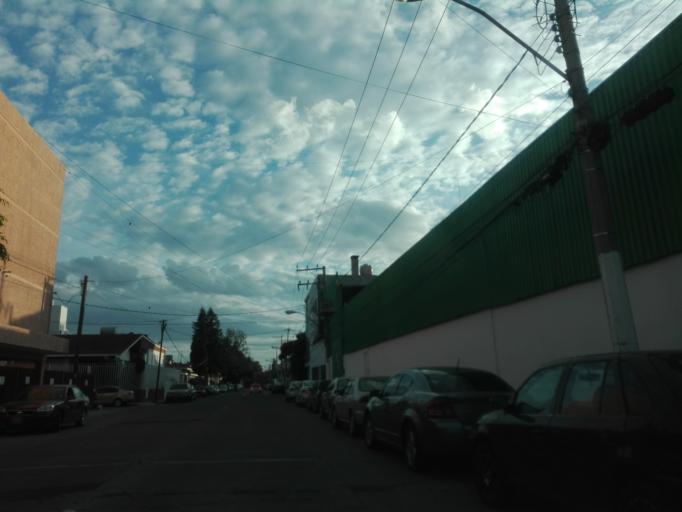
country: MX
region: Guanajuato
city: Leon
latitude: 21.1167
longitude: -101.6624
